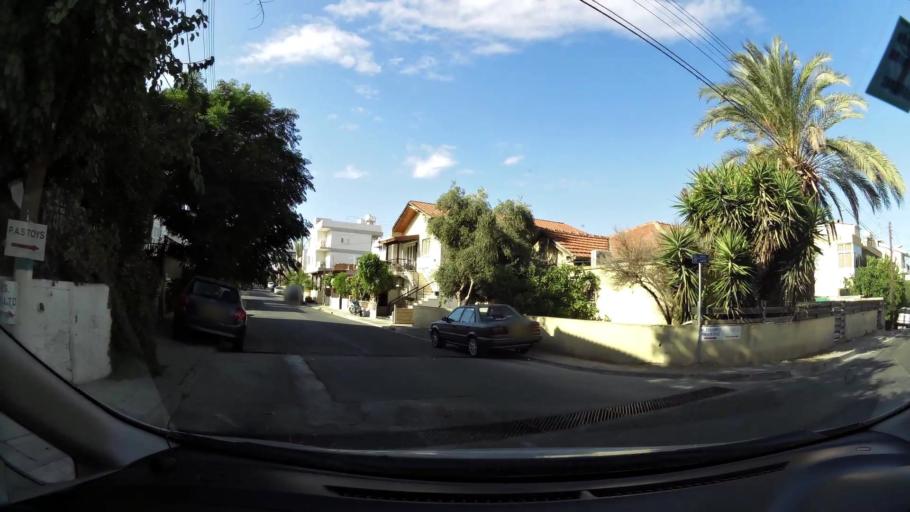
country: CY
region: Lefkosia
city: Nicosia
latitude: 35.1367
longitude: 33.3486
